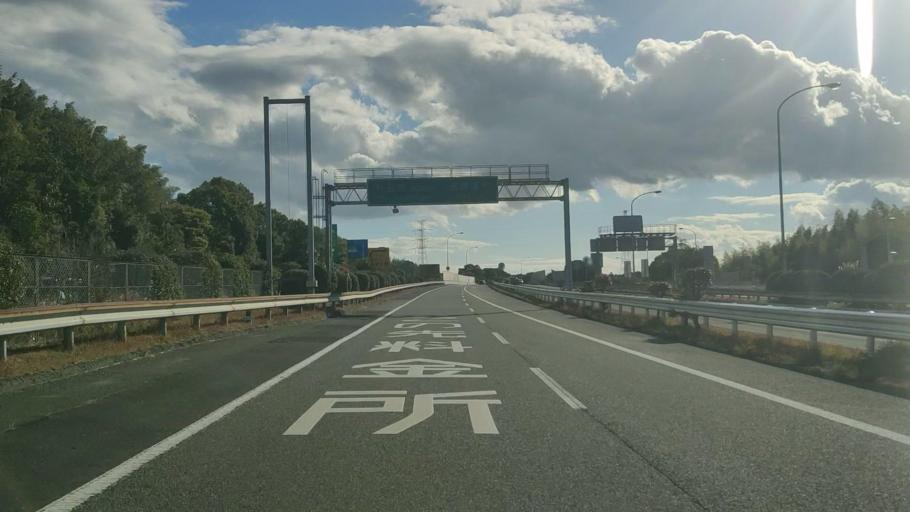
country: JP
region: Fukuoka
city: Nogata
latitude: 33.7863
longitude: 130.7462
